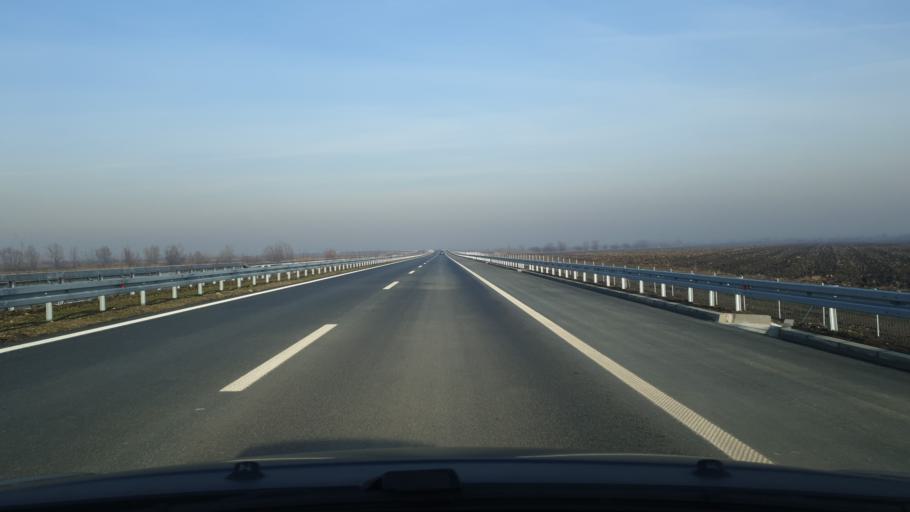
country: RS
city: Baric
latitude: 44.6788
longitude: 20.2594
